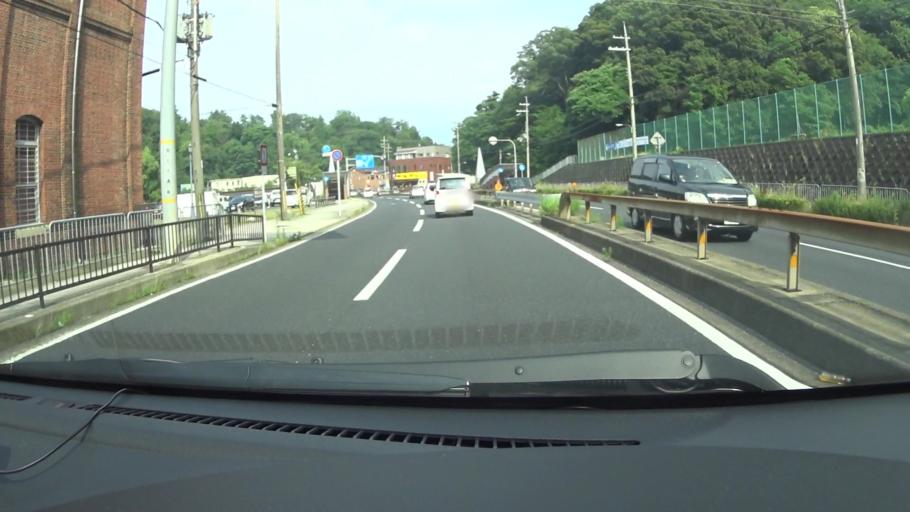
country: JP
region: Kyoto
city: Kameoka
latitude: 35.0611
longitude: 135.5298
